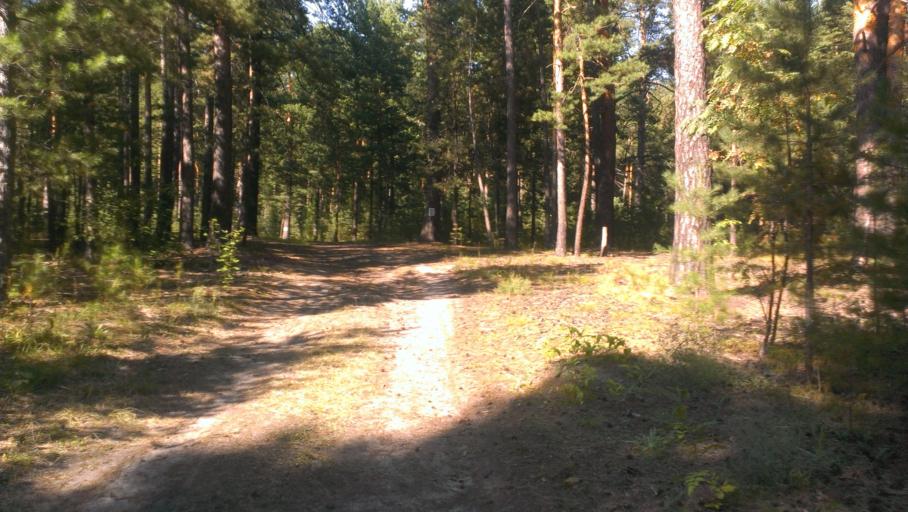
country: RU
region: Altai Krai
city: Novosilikatnyy
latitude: 53.3150
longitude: 83.6850
